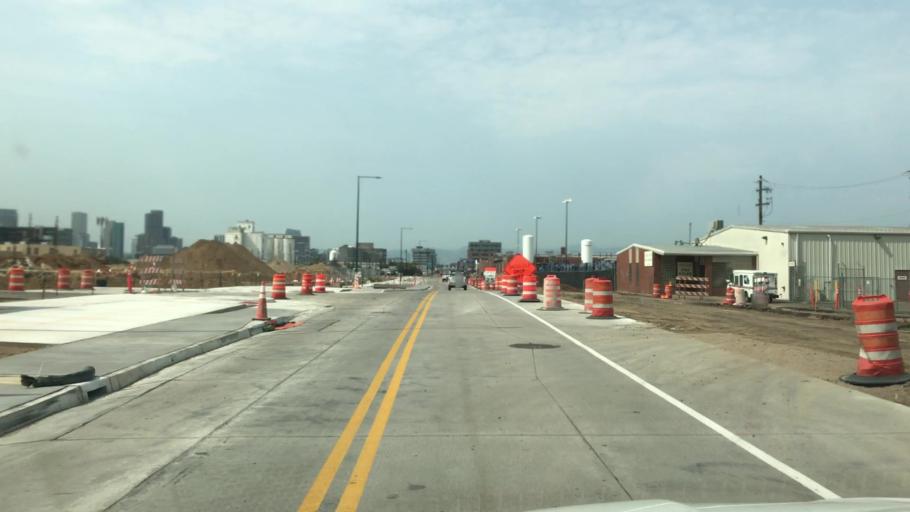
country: US
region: Colorado
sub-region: Denver County
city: Denver
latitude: 39.7762
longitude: -104.9712
